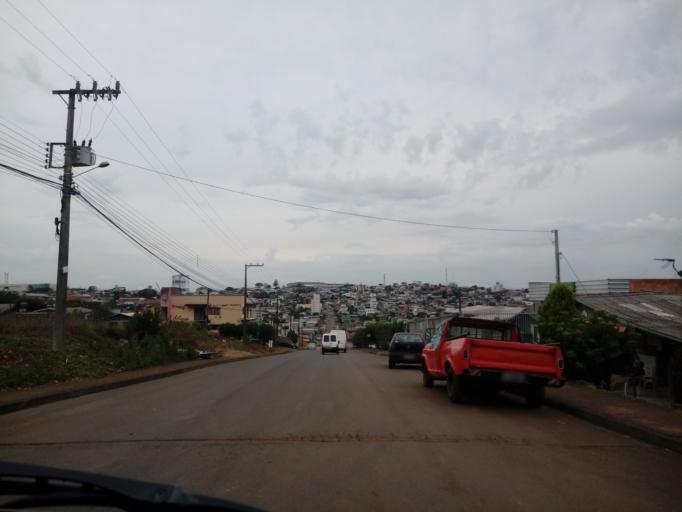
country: BR
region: Santa Catarina
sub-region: Chapeco
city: Chapeco
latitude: -27.0645
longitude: -52.6354
